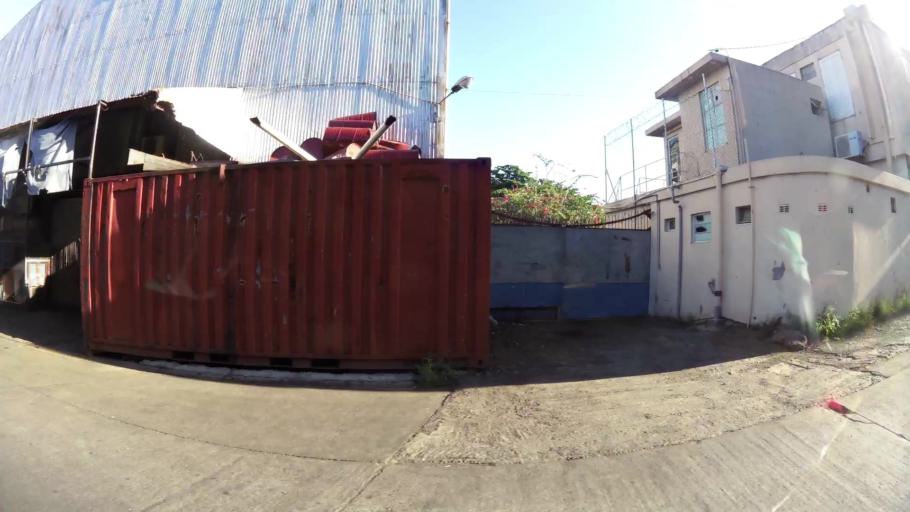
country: MU
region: Port Louis
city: Port Louis
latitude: -20.1558
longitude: 57.5049
